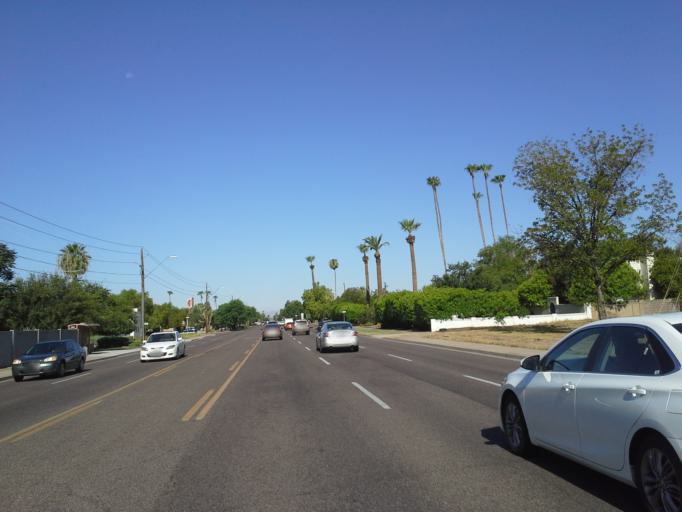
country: US
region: Arizona
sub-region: Maricopa County
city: Phoenix
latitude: 33.5528
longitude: -112.0679
